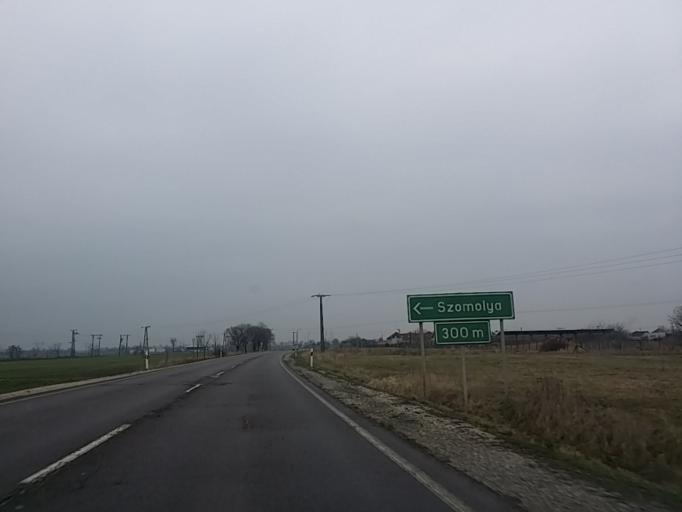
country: HU
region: Borsod-Abauj-Zemplen
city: Mezokovesd
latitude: 47.8171
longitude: 20.5507
